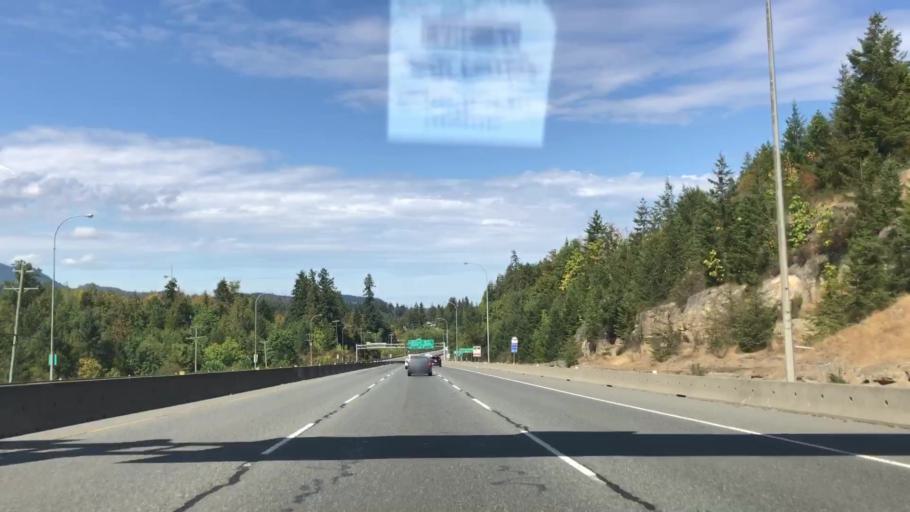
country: CA
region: British Columbia
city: Nanaimo
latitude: 49.1157
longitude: -123.9085
